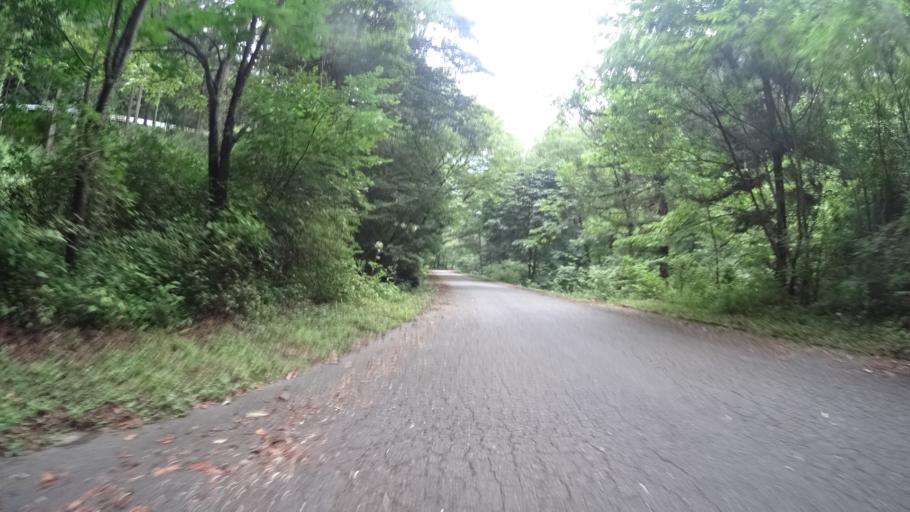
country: JP
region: Yamanashi
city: Kofu-shi
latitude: 35.8082
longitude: 138.5879
